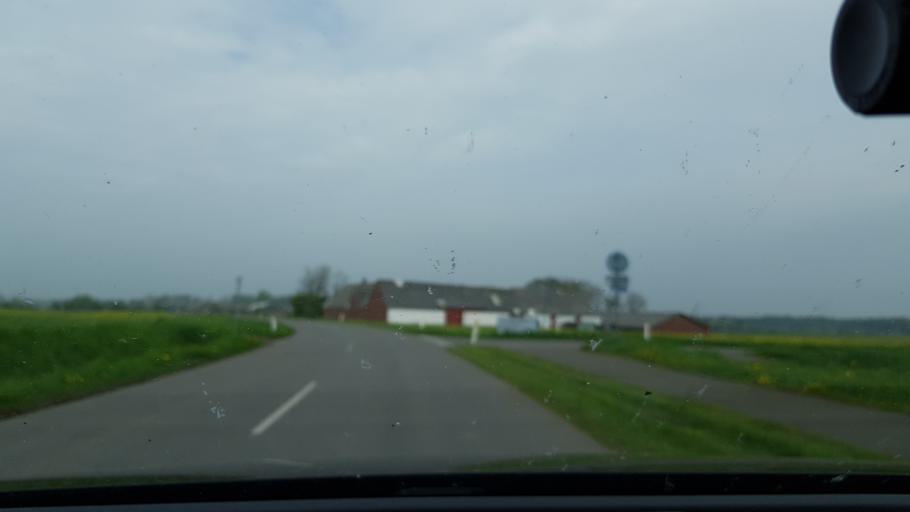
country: DK
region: Capital Region
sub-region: Bornholm Kommune
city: Nexo
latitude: 55.0101
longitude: 15.0952
